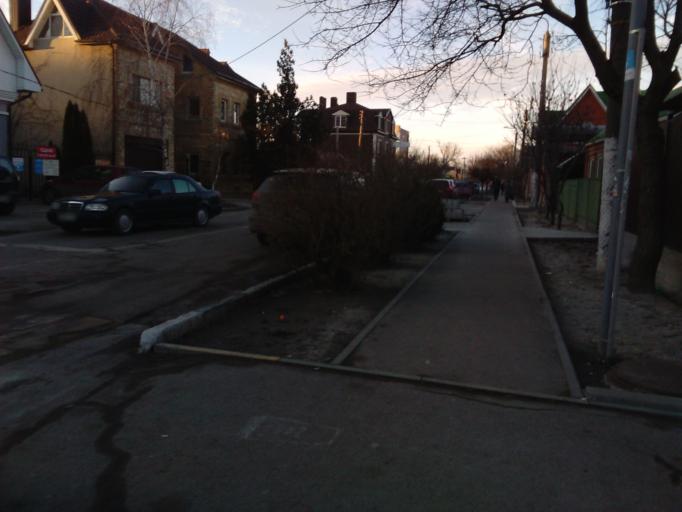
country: RU
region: Rostov
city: Bataysk
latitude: 47.1403
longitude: 39.7450
